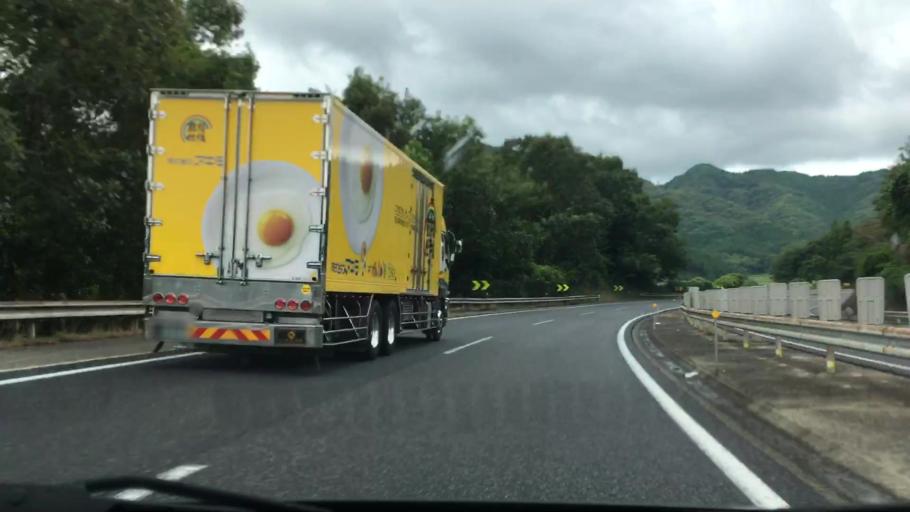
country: JP
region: Okayama
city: Takahashi
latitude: 34.9855
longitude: 133.7124
